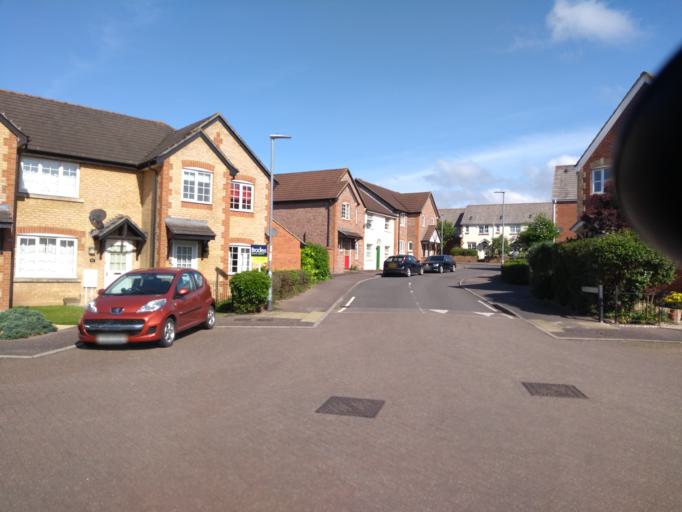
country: GB
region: England
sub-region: Somerset
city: Taunton
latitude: 51.0336
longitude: -3.0845
